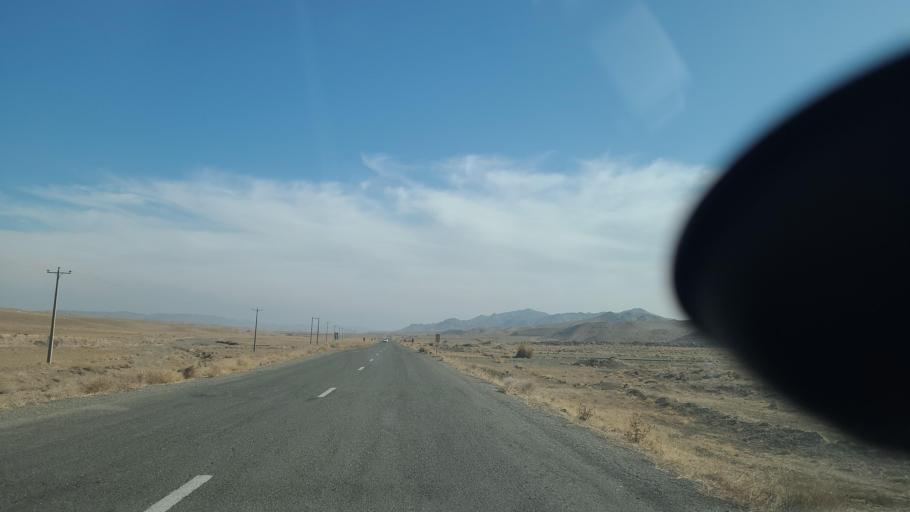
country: IR
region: Razavi Khorasan
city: Fariman
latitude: 35.5886
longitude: 59.6284
